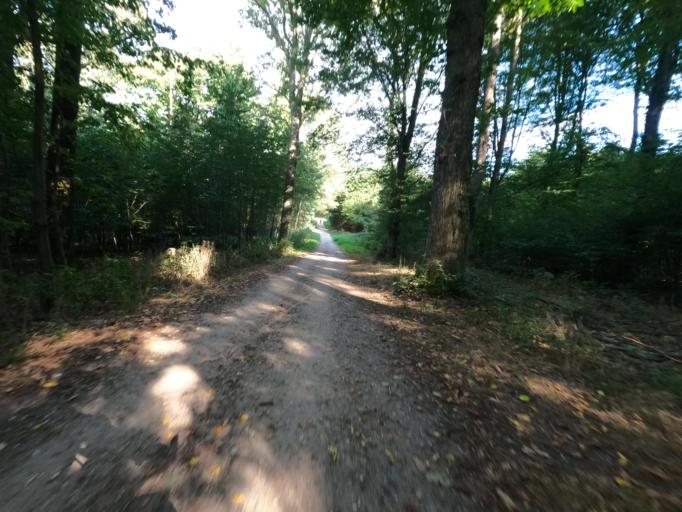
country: DE
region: North Rhine-Westphalia
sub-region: Regierungsbezirk Koln
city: Wassenberg
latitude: 51.0933
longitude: 6.1693
